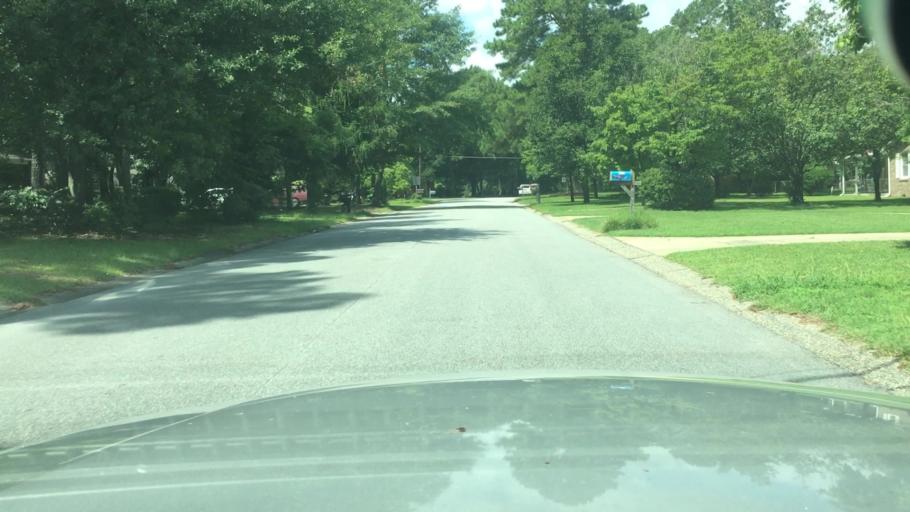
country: US
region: North Carolina
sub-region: Cumberland County
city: Hope Mills
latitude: 35.0325
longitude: -78.9890
